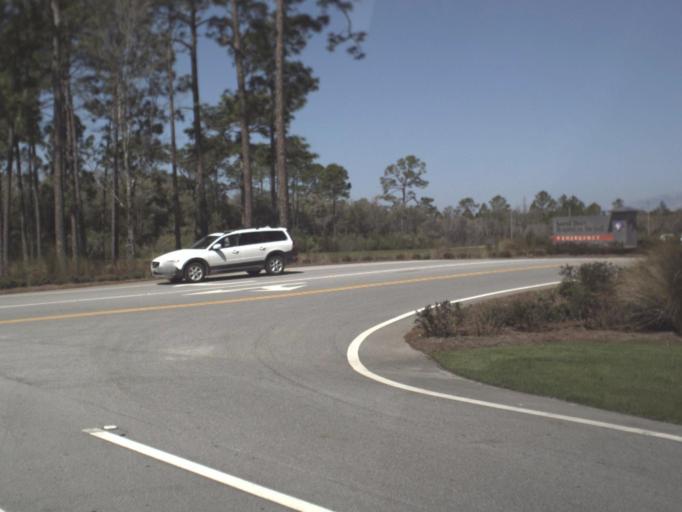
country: US
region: Florida
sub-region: Gulf County
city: Port Saint Joe
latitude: 29.7766
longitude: -85.2874
